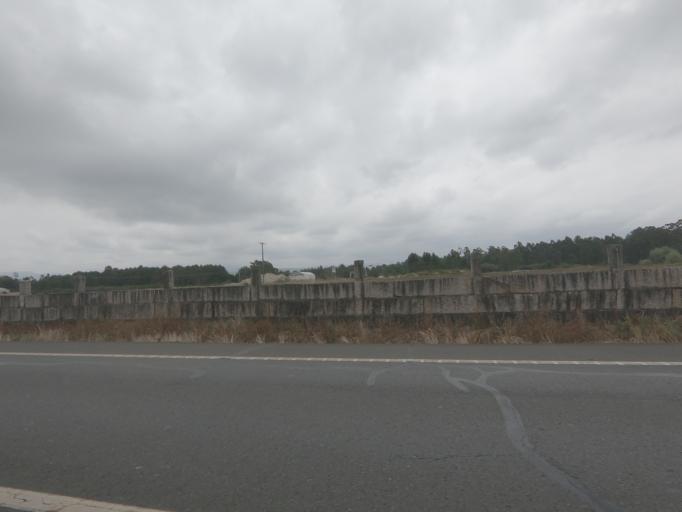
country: ES
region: Galicia
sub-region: Provincia de Pontevedra
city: Tomino
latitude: 41.9895
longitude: -8.7144
